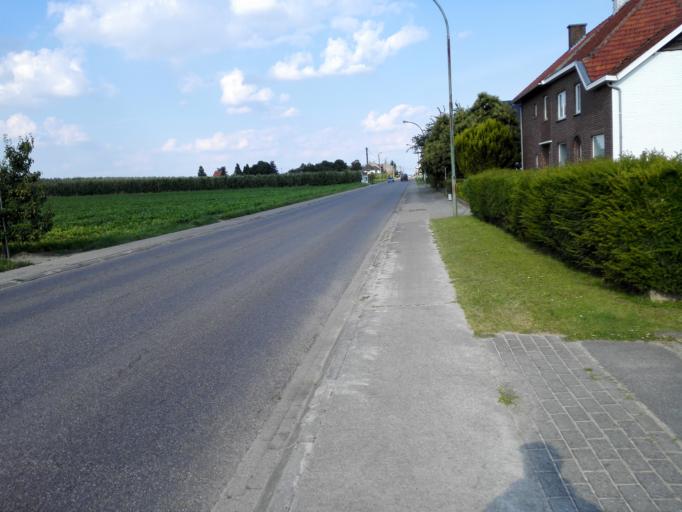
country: BE
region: Flanders
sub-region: Provincie Vlaams-Brabant
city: Tienen
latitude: 50.8212
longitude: 4.9558
